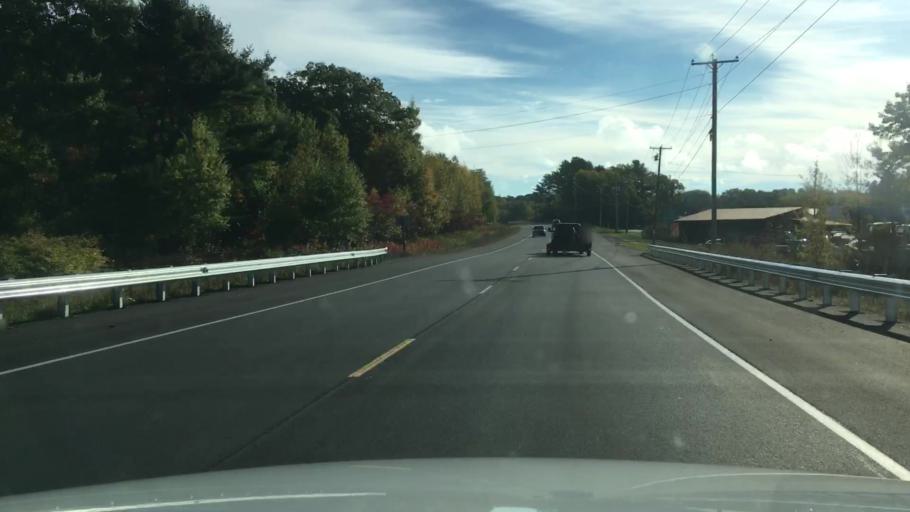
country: US
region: Maine
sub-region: Knox County
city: Thomaston
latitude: 44.0784
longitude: -69.2183
